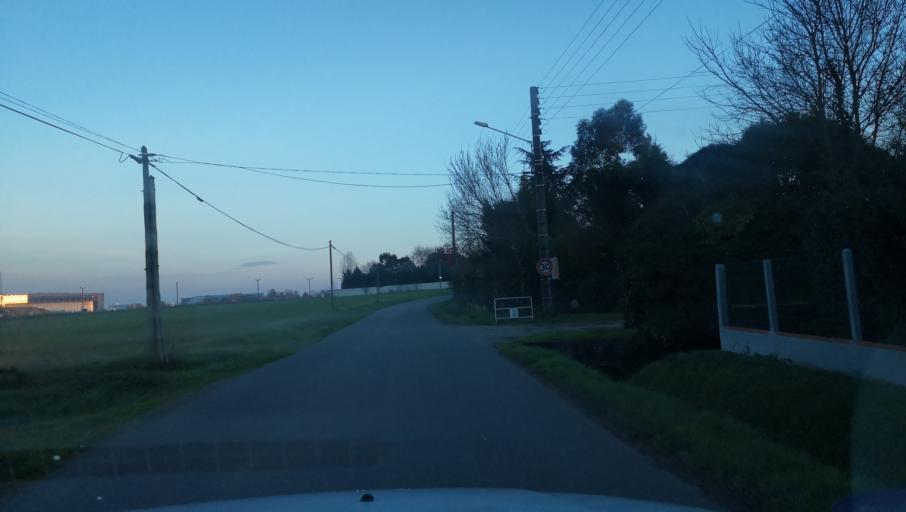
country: FR
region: Midi-Pyrenees
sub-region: Departement de la Haute-Garonne
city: Cornebarrieu
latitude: 43.6640
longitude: 1.3442
